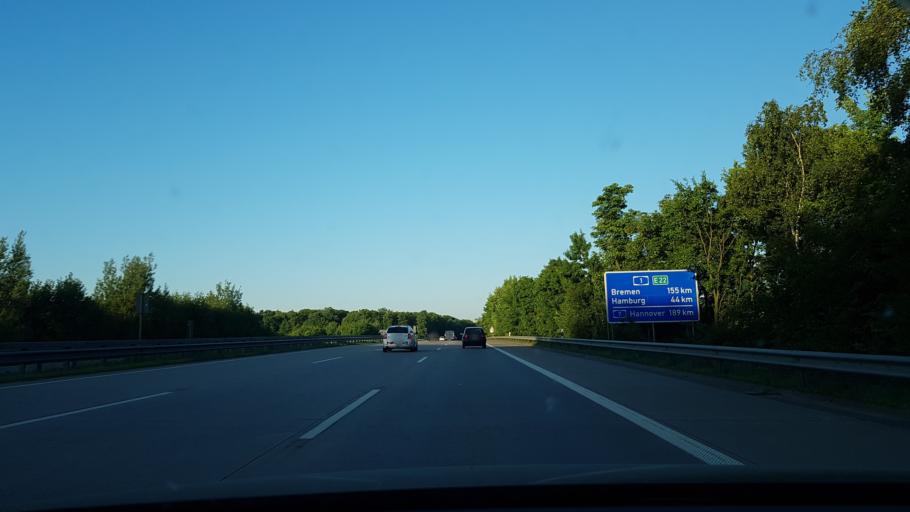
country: DE
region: Schleswig-Holstein
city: Politz
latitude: 53.7803
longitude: 10.4121
